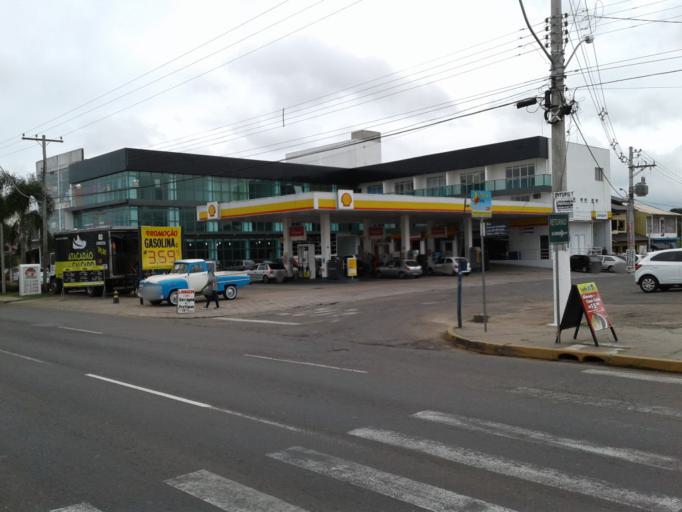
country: BR
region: Rio Grande do Sul
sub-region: Gravatai
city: Gravatai
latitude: -29.9355
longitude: -51.0423
